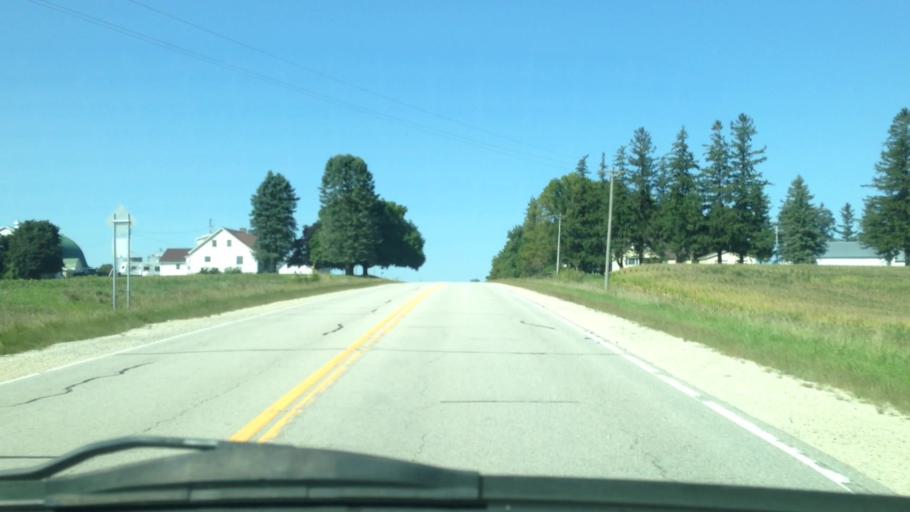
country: US
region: Minnesota
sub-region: Houston County
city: Spring Grove
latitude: 43.6064
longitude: -91.7902
